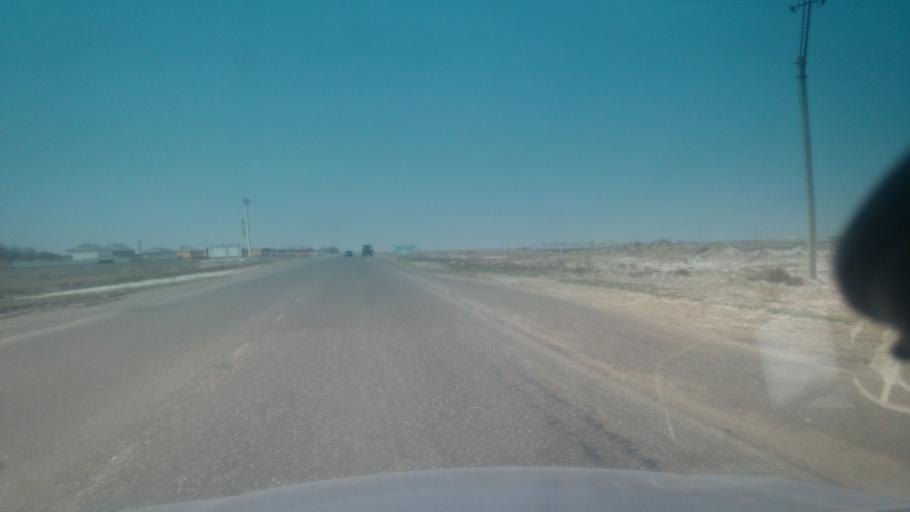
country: UZ
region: Jizzax
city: Dashtobod
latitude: 40.1661
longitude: 68.6032
